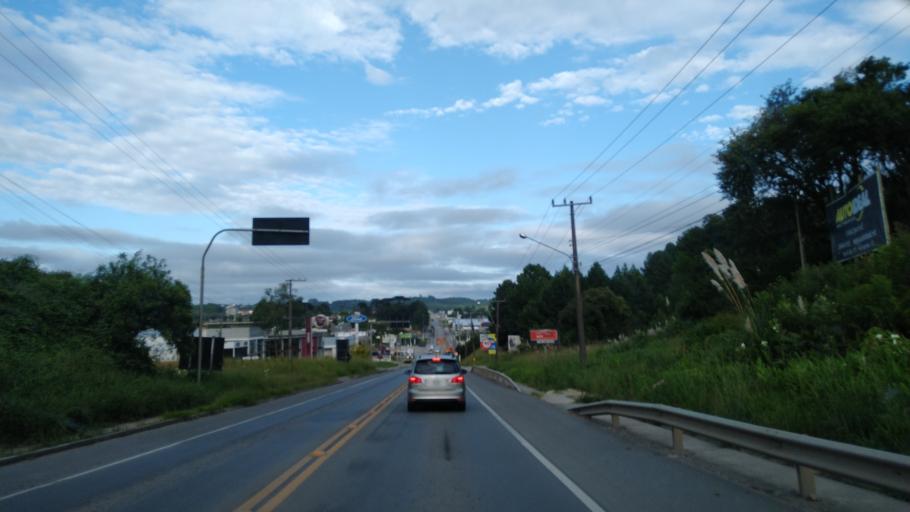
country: BR
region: Santa Catarina
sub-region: Sao Bento Do Sul
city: Sao Bento do Sul
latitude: -26.2237
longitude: -49.3945
